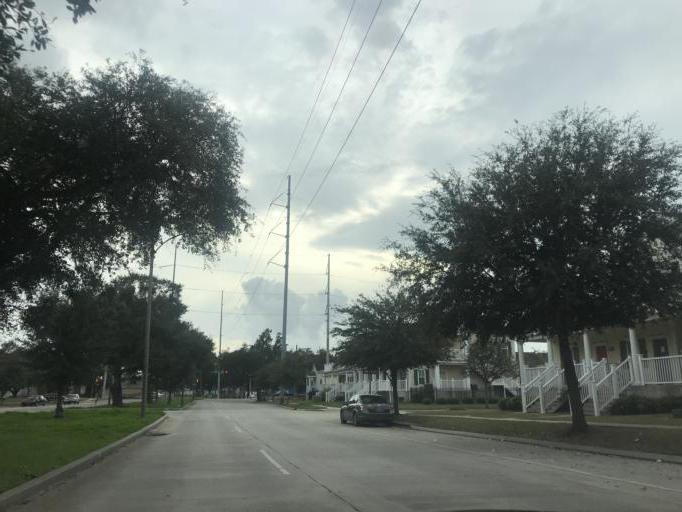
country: US
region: Louisiana
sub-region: Orleans Parish
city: New Orleans
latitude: 29.9501
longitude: -90.0924
